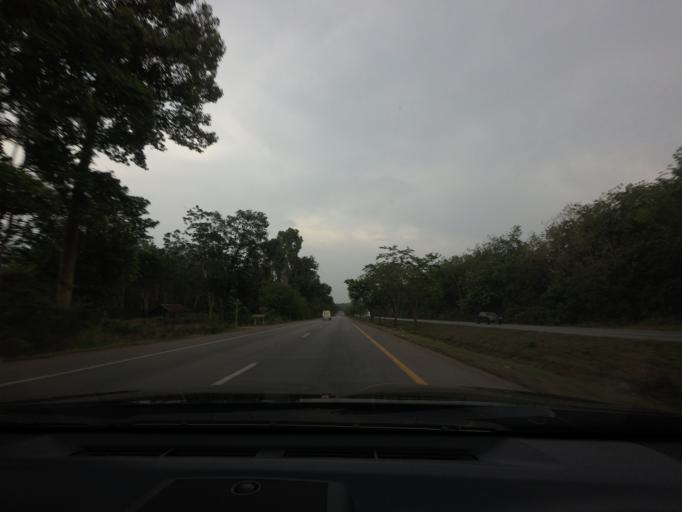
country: TH
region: Surat Thani
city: Chaiya
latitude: 9.4715
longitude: 99.1493
